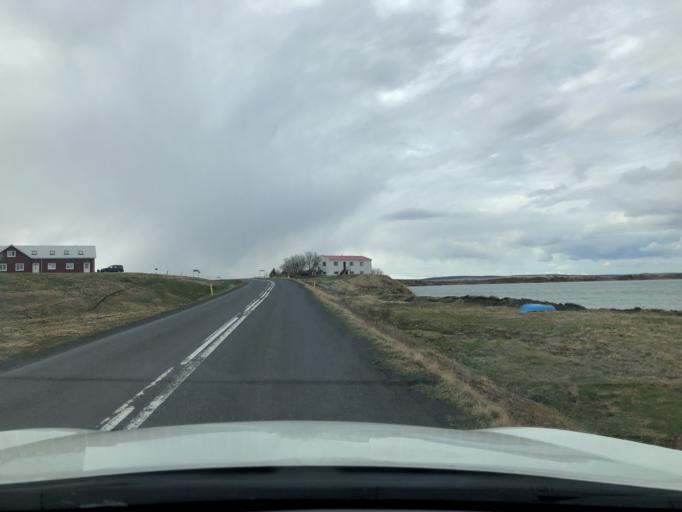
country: IS
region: Northeast
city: Laugar
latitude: 65.5688
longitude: -17.0435
